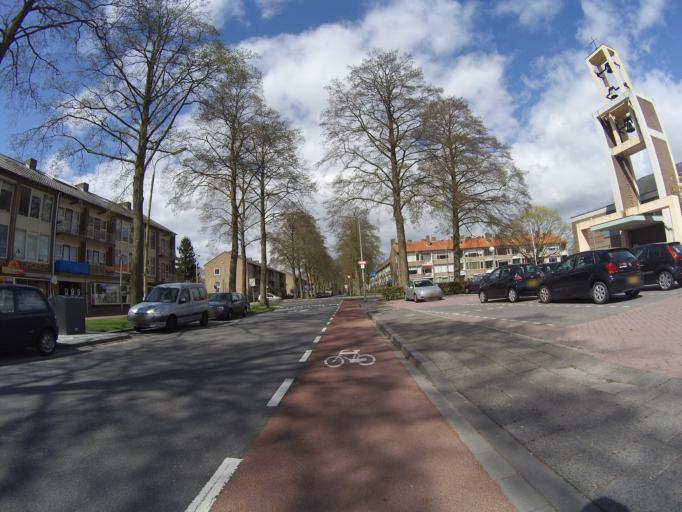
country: NL
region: Utrecht
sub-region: Gemeente Amersfoort
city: Randenbroek
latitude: 52.1489
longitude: 5.4047
